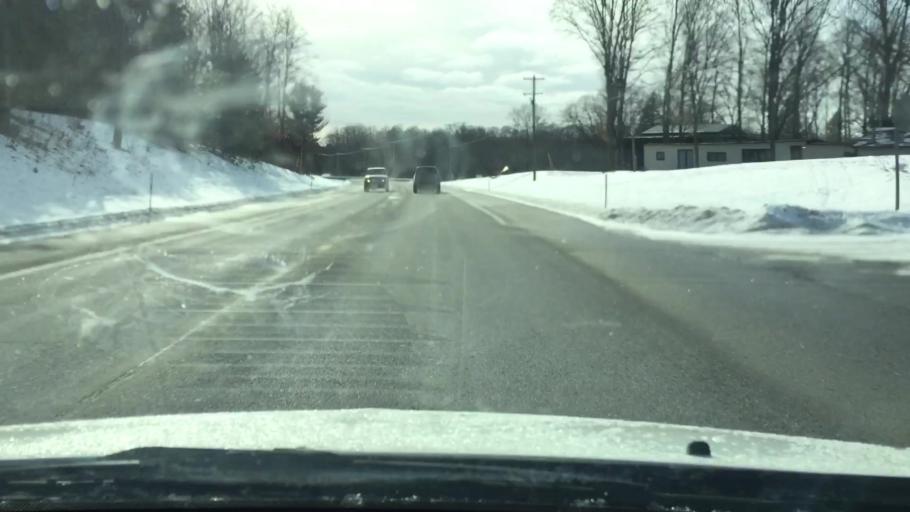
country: US
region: Michigan
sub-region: Wexford County
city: Manton
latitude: 44.5840
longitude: -85.3571
